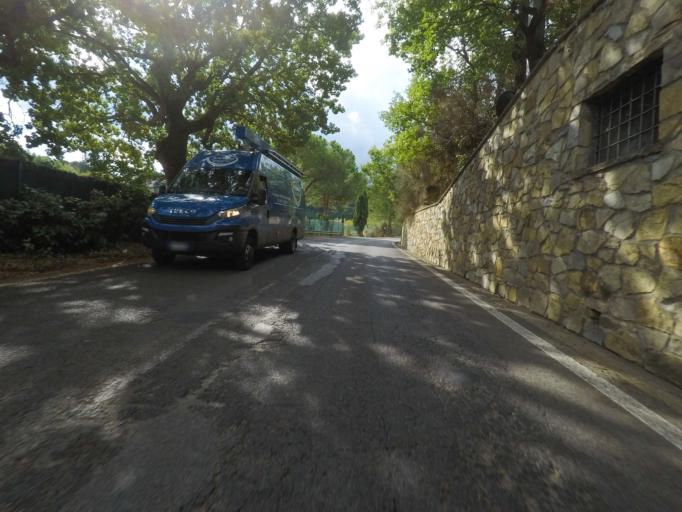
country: IT
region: Tuscany
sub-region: Provincia di Siena
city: Montepulciano
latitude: 43.1143
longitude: 11.7903
